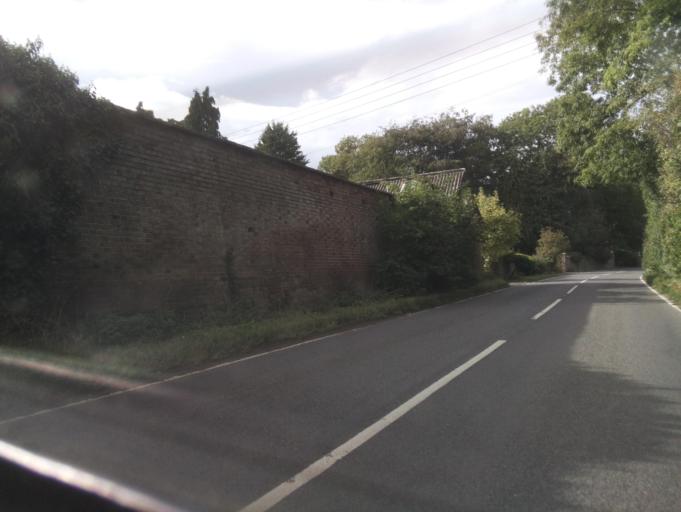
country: GB
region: England
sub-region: Telford and Wrekin
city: Madeley
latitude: 52.6266
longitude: -2.4134
